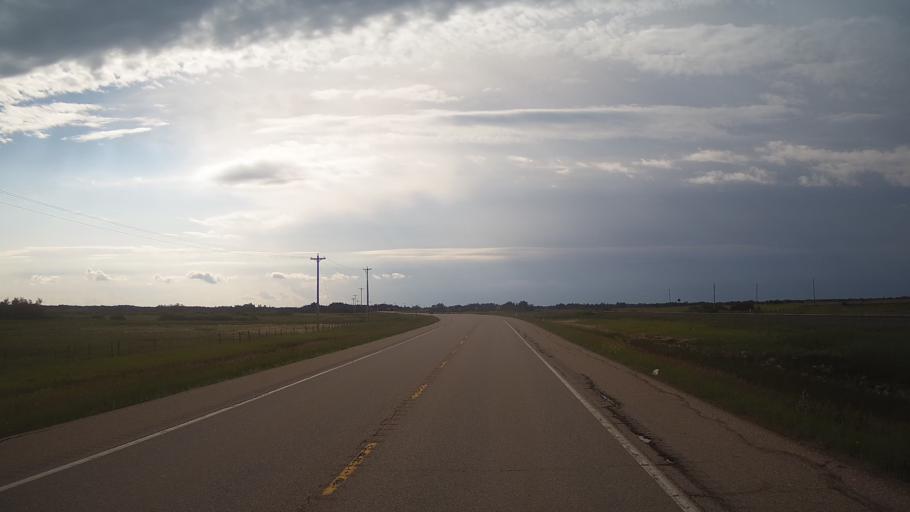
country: CA
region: Alberta
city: Viking
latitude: 53.1301
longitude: -111.9036
